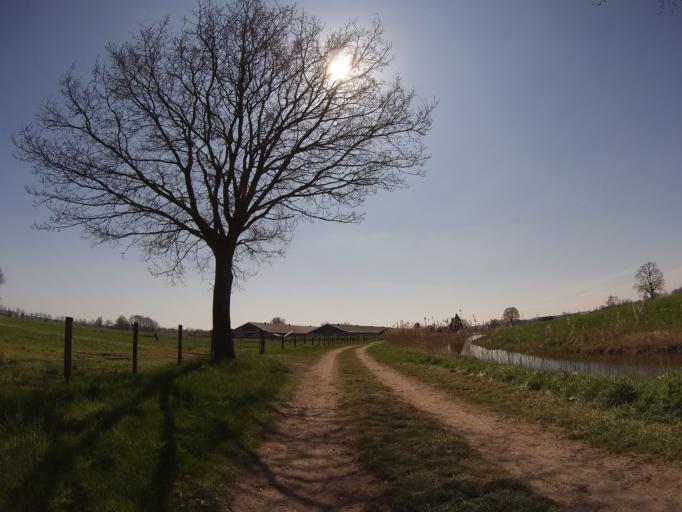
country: NL
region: Utrecht
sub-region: Gemeente Utrechtse Heuvelrug
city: Overberg
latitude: 52.0564
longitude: 5.4838
